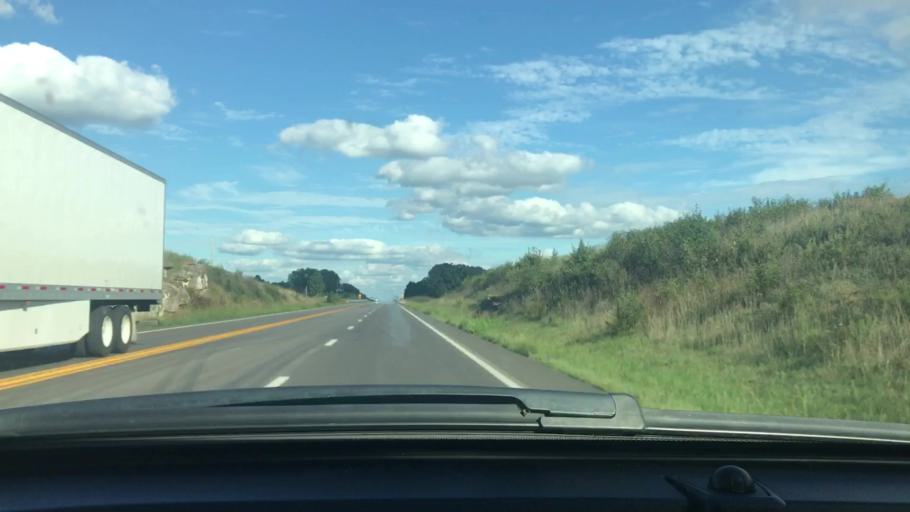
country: US
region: Missouri
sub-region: Oregon County
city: Thayer
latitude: 36.5850
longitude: -91.6199
